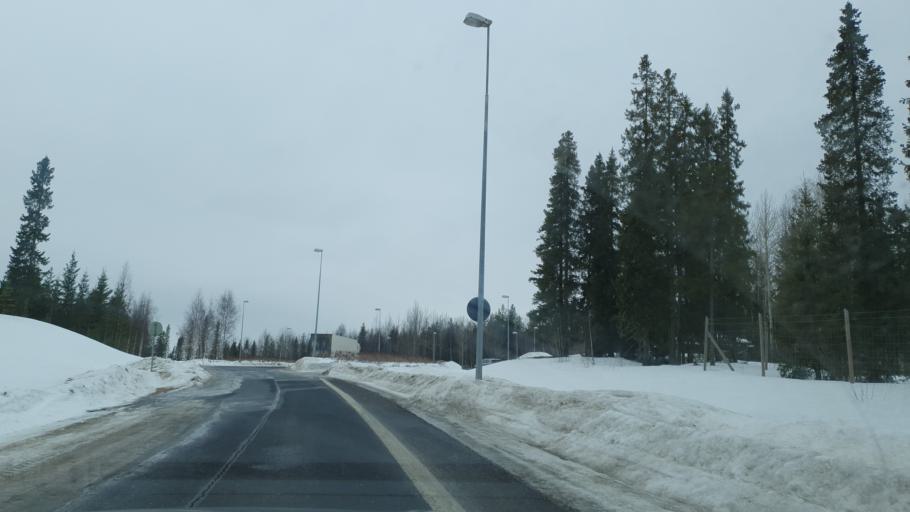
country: FI
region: Lapland
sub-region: Kemi-Tornio
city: Keminmaa
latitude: 65.8265
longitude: 24.4120
